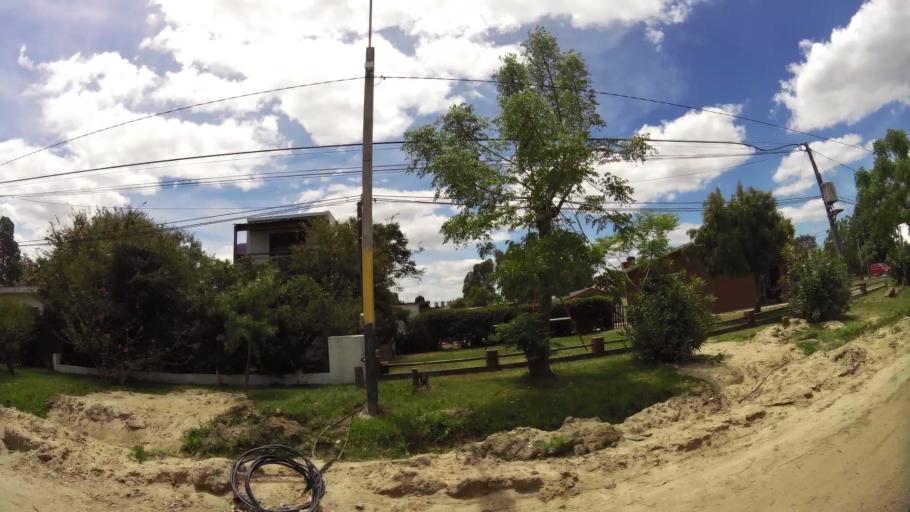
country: UY
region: Canelones
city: Barra de Carrasco
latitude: -34.8320
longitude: -55.9800
